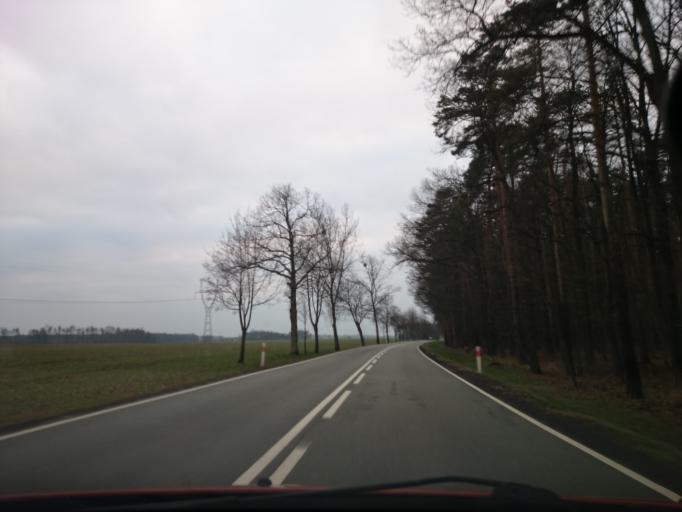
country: PL
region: Opole Voivodeship
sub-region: Powiat opolski
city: Niemodlin
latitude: 50.6136
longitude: 17.5652
